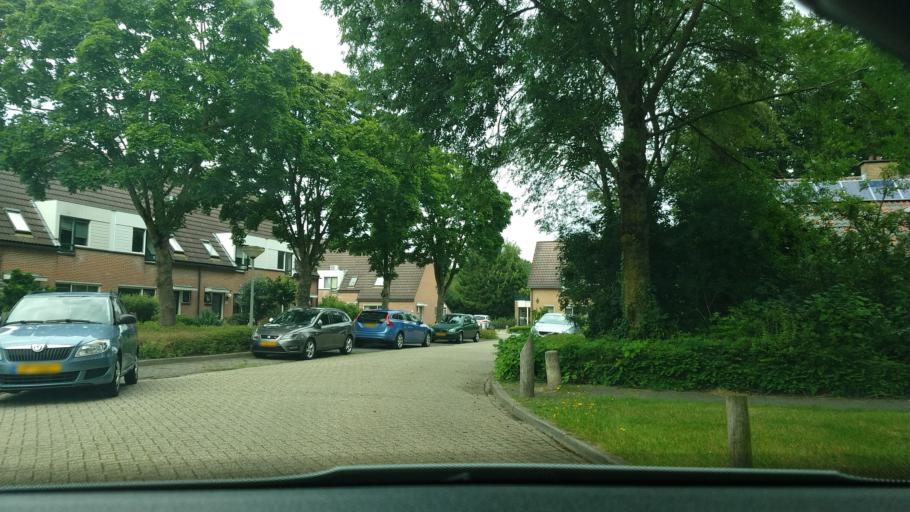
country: NL
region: Gelderland
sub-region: Gemeente Ermelo
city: Ermelo
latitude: 52.2999
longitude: 5.6030
